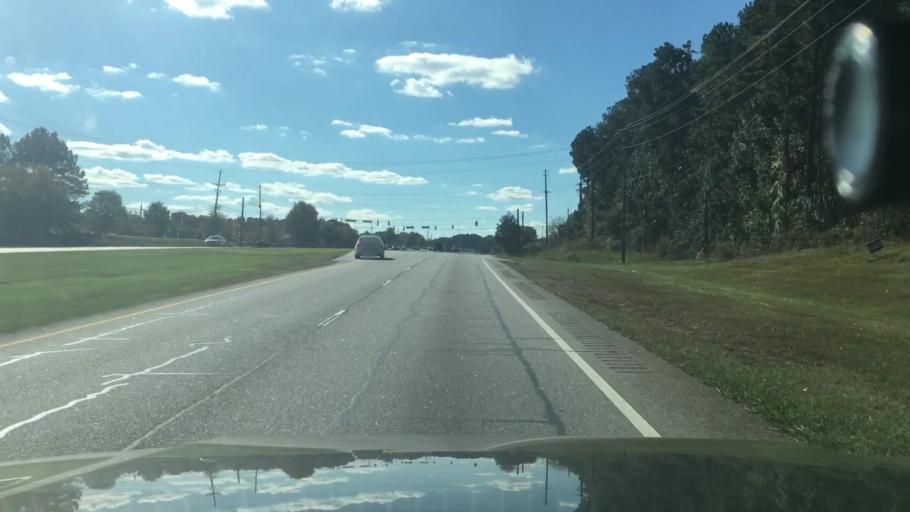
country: US
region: Georgia
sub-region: Coweta County
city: East Newnan
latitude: 33.3987
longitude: -84.7367
